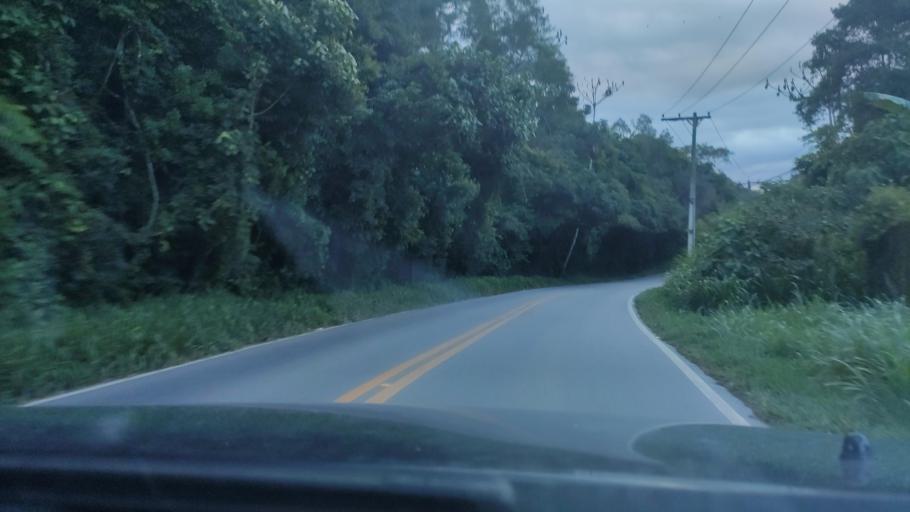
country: BR
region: Sao Paulo
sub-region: Campos Do Jordao
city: Campos do Jordao
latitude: -22.8244
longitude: -45.6757
